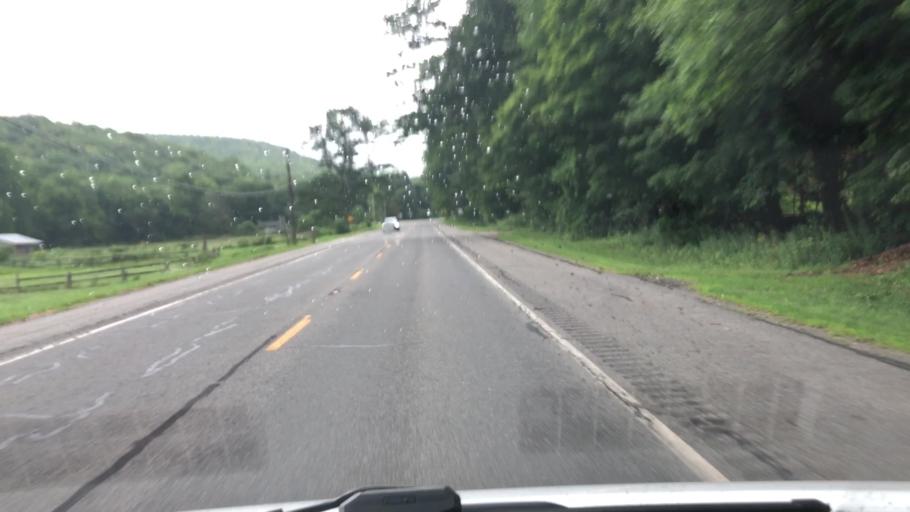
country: US
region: Massachusetts
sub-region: Berkshire County
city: Williamstown
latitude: 42.6333
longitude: -73.2258
